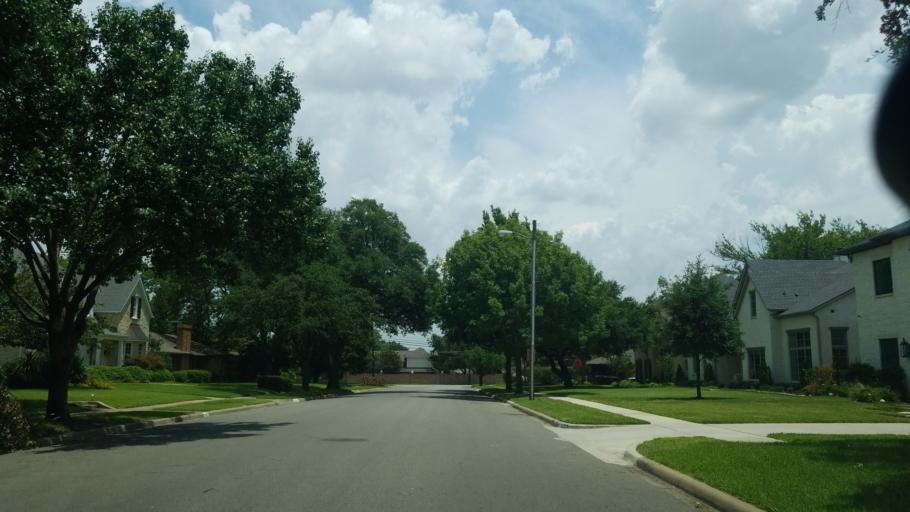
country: US
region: Texas
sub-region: Dallas County
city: University Park
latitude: 32.8706
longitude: -96.7881
